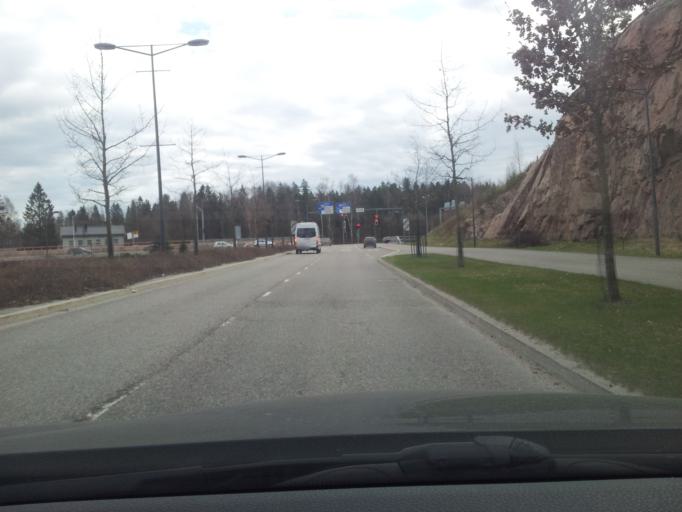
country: FI
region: Uusimaa
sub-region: Helsinki
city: Kauniainen
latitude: 60.1826
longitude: 24.7450
